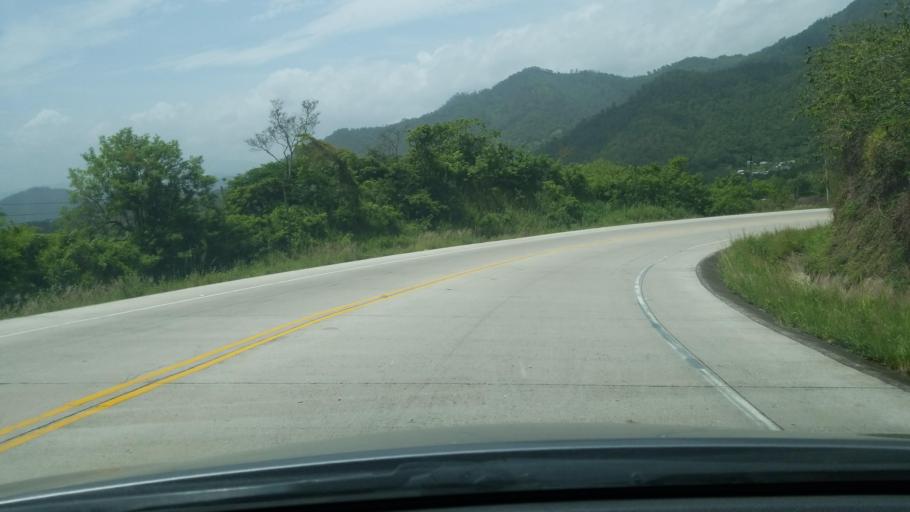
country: HN
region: Copan
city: Quezailica
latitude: 14.8992
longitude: -88.7562
